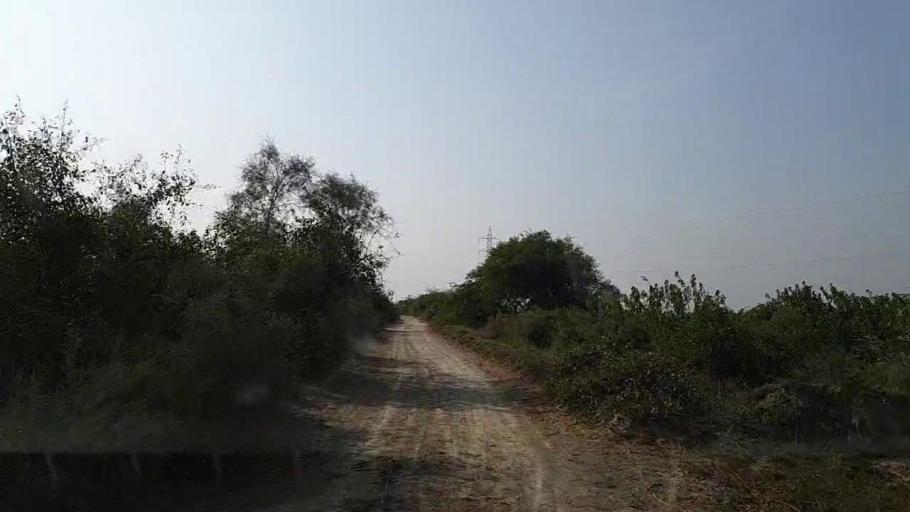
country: PK
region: Sindh
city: Mirpur Sakro
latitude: 24.5754
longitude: 67.5810
